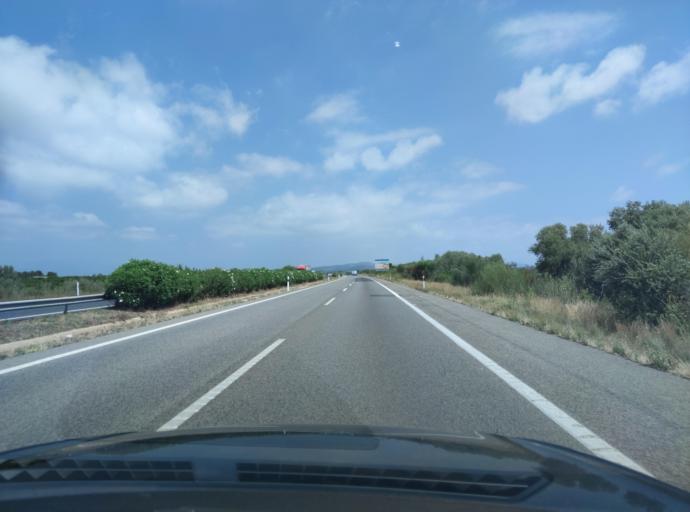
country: ES
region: Catalonia
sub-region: Provincia de Tarragona
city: Alcanar
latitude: 40.5297
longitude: 0.4187
